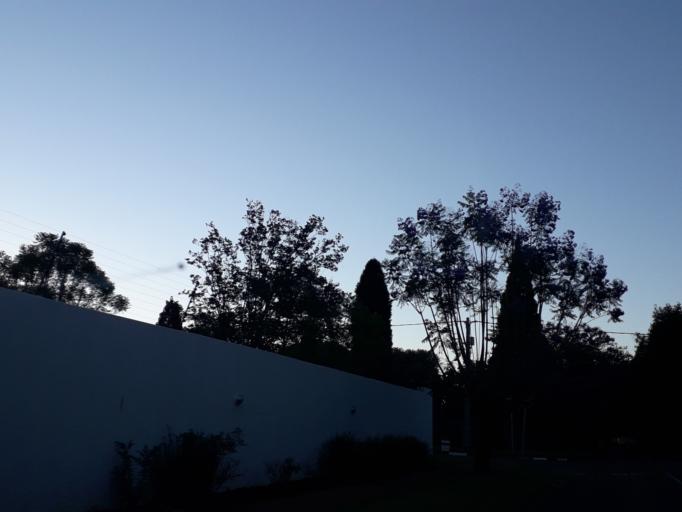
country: ZA
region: Gauteng
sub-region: City of Johannesburg Metropolitan Municipality
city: Roodepoort
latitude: -26.1261
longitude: 27.9461
